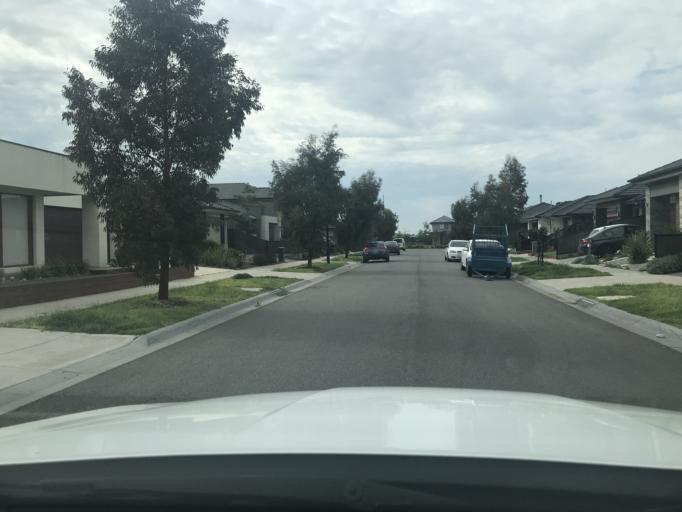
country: AU
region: Victoria
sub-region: Hume
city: Roxburgh Park
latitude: -37.6026
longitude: 144.9019
